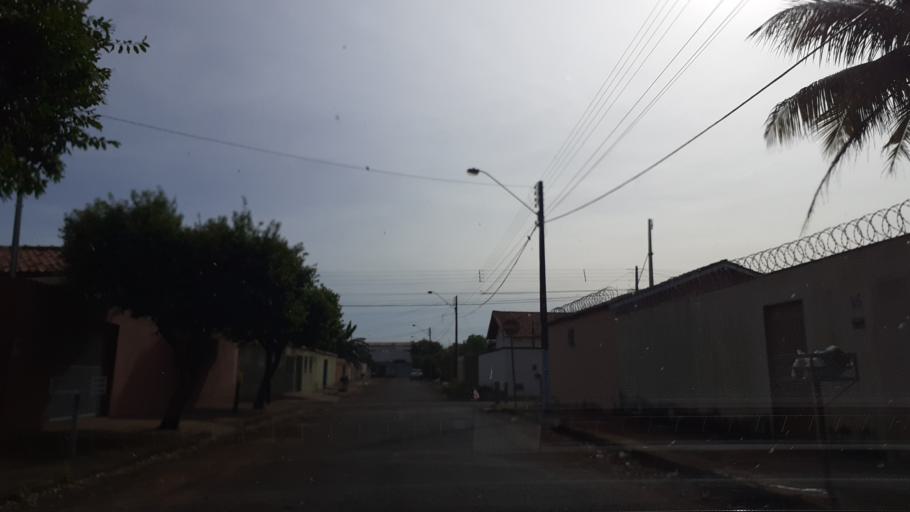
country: BR
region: Goias
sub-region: Itumbiara
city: Itumbiara
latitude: -18.4160
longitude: -49.2451
